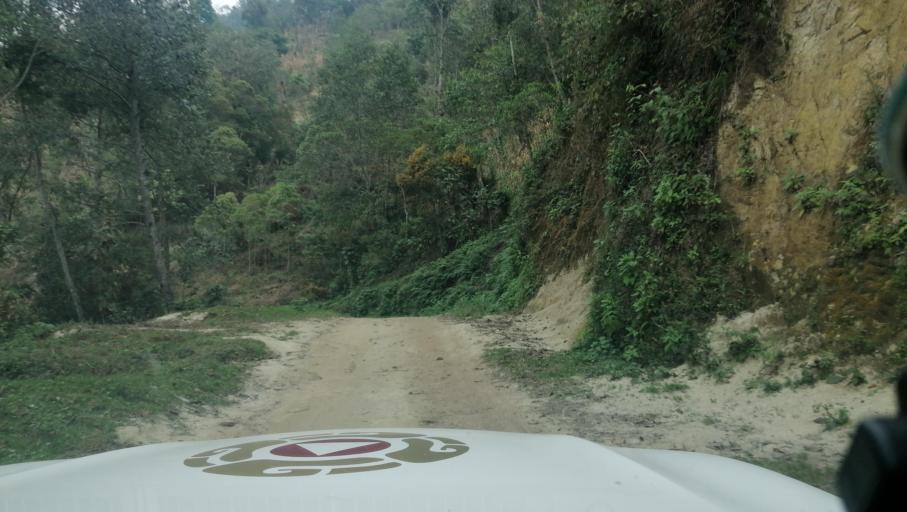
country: GT
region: San Marcos
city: Tacana
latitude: 15.2049
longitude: -92.1688
